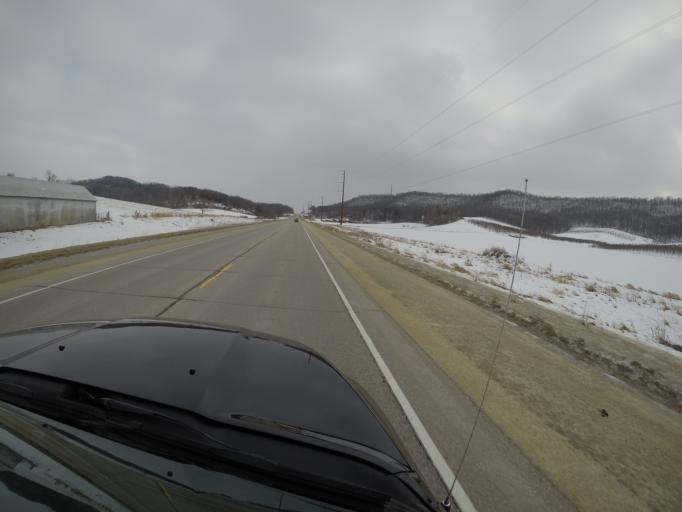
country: US
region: Wisconsin
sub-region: Trempealeau County
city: Galesville
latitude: 44.0749
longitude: -91.3394
